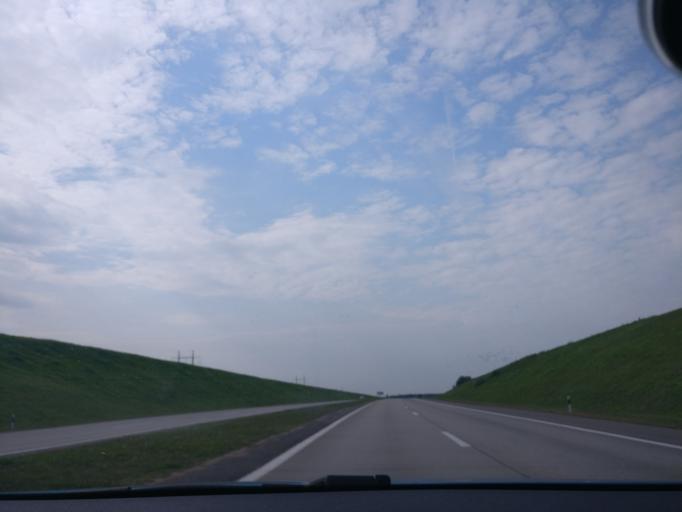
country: BY
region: Minsk
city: Astrashytski Haradok
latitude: 54.0998
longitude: 27.7905
